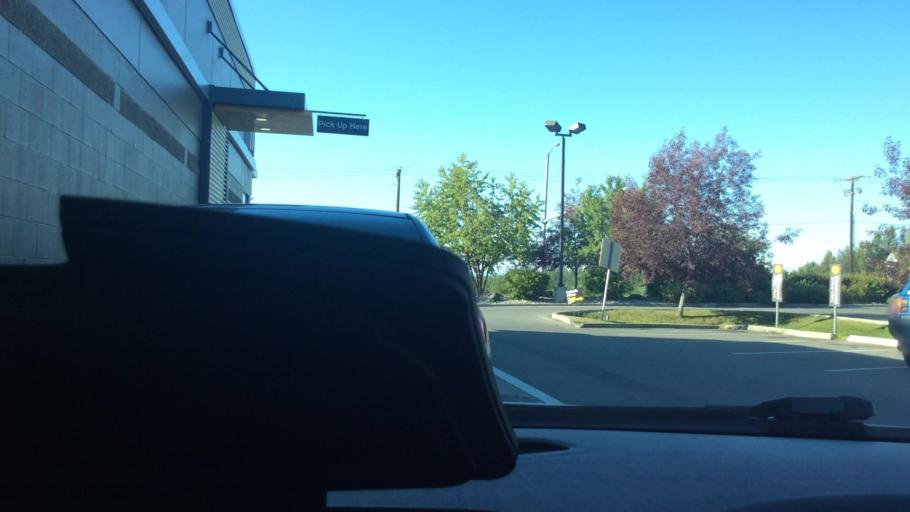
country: US
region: Alaska
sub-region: Anchorage Municipality
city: Anchorage
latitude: 61.2092
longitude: -149.7749
